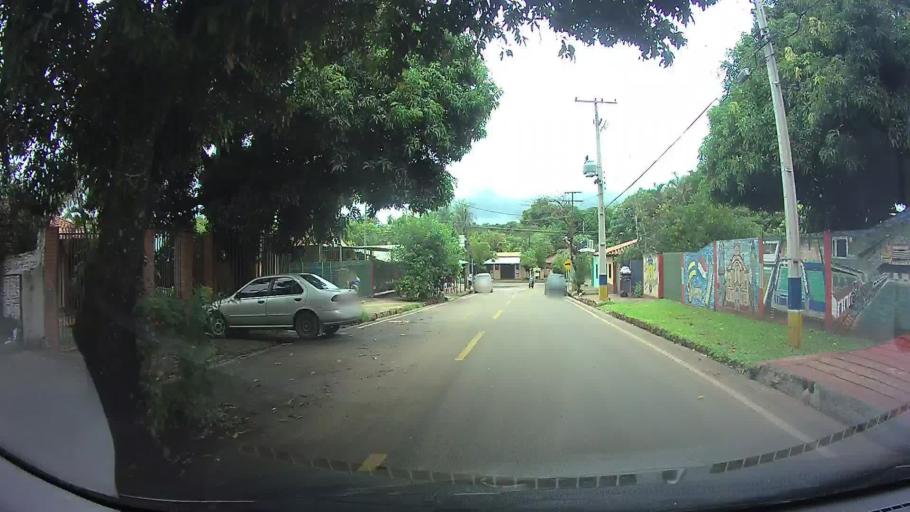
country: PY
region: Central
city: San Lorenzo
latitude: -25.2773
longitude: -57.4863
